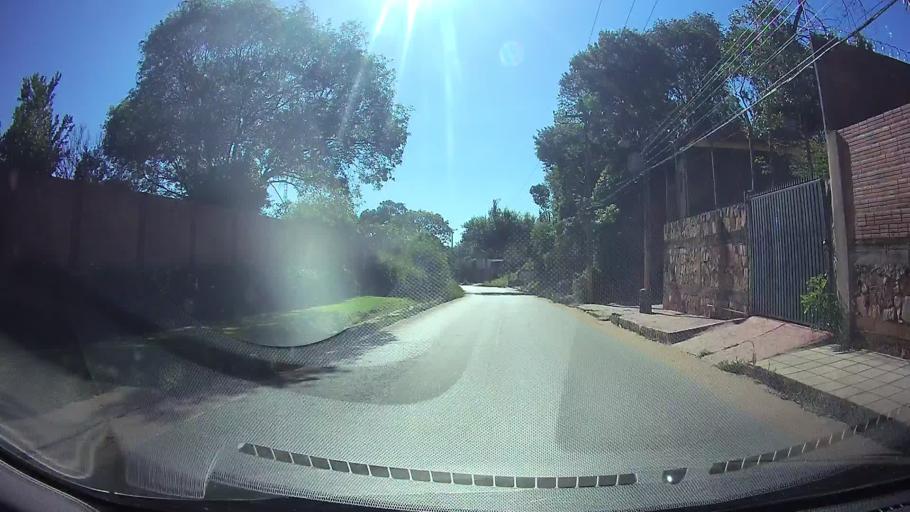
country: PY
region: Central
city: Fernando de la Mora
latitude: -25.2965
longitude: -57.5289
